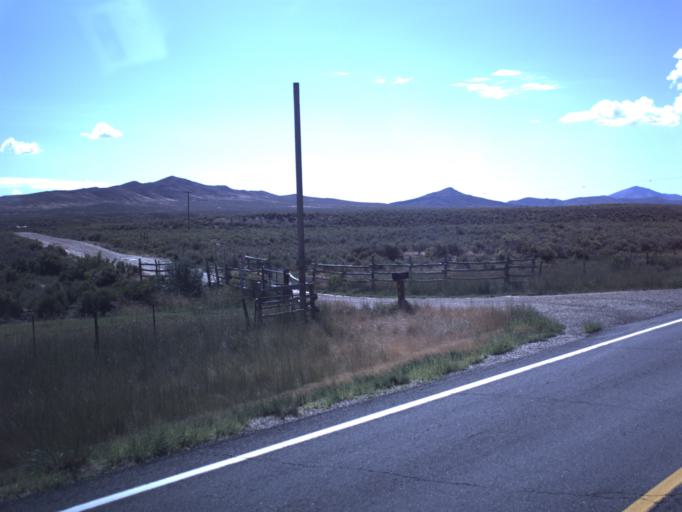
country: US
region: Utah
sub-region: Tooele County
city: Tooele
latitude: 40.1625
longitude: -112.4308
